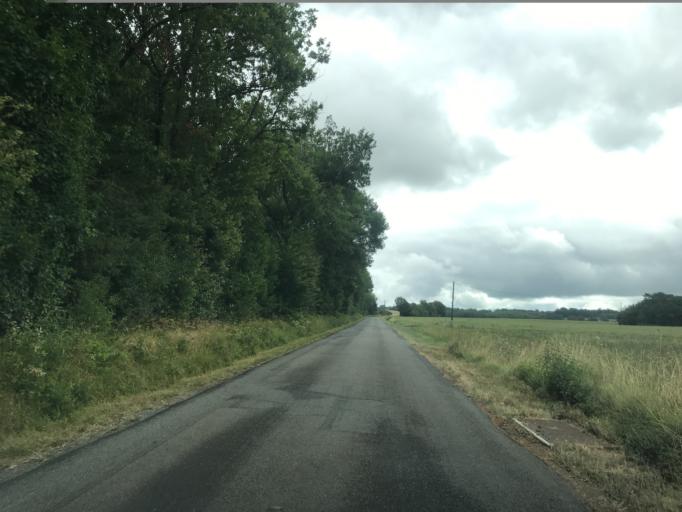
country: FR
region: Poitou-Charentes
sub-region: Departement de la Charente
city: Dignac
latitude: 45.5575
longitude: 0.2461
